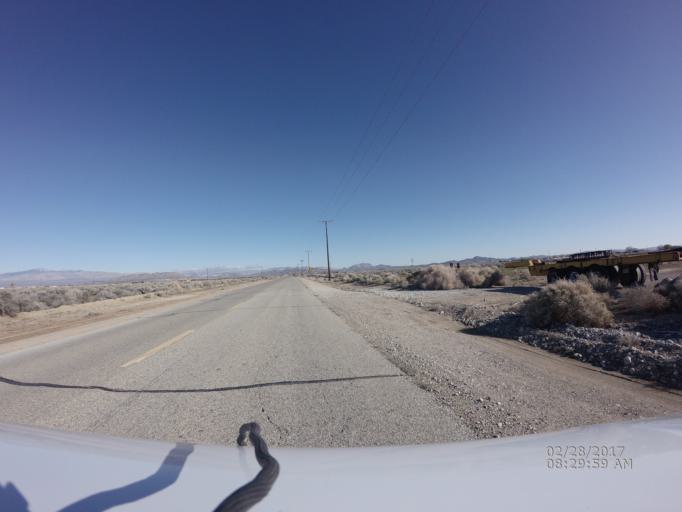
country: US
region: California
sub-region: Kern County
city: Rosamond
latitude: 34.8177
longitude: -118.2376
